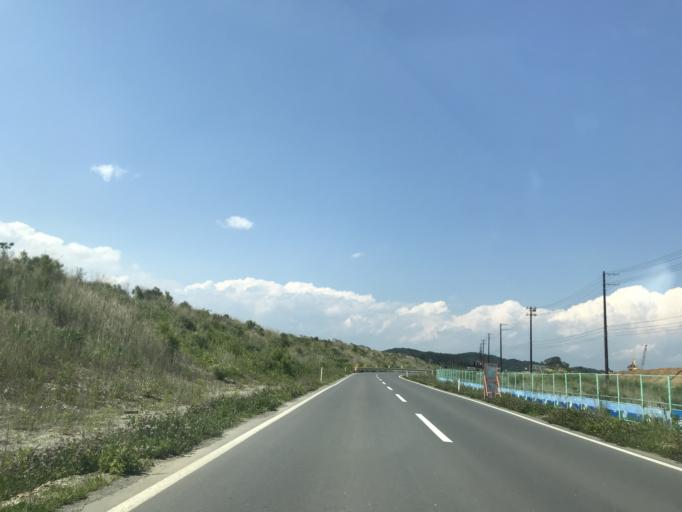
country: JP
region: Miyagi
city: Yamoto
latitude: 38.3596
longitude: 141.1559
